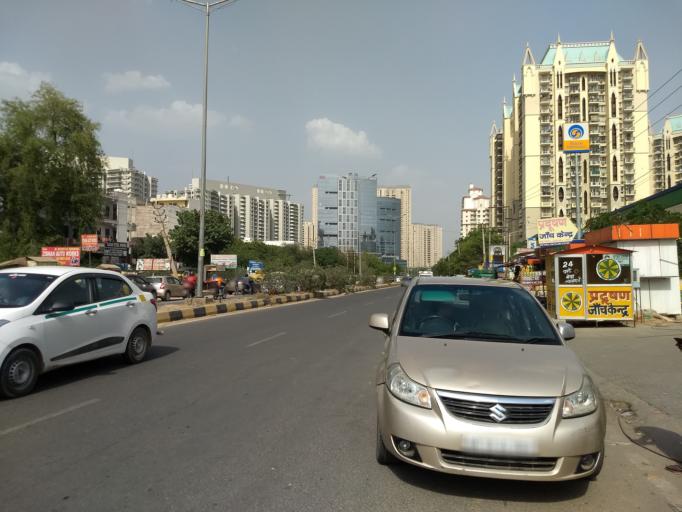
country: IN
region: Haryana
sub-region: Gurgaon
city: Gurgaon
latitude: 28.4499
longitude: 77.0908
